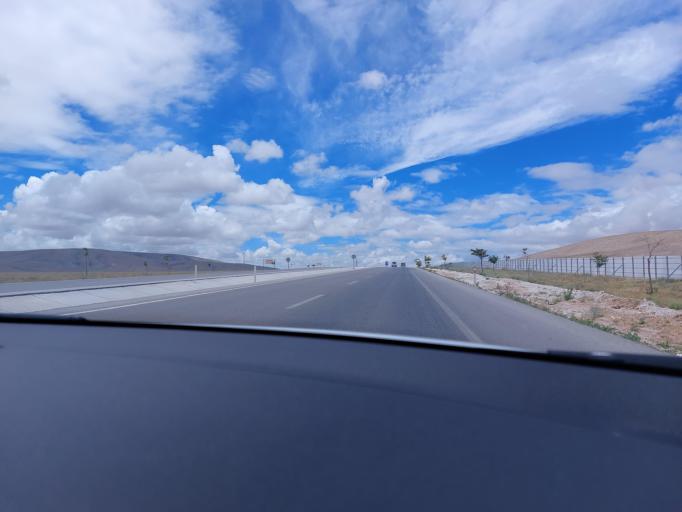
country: TR
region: Konya
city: Obruk
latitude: 38.0621
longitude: 33.0522
